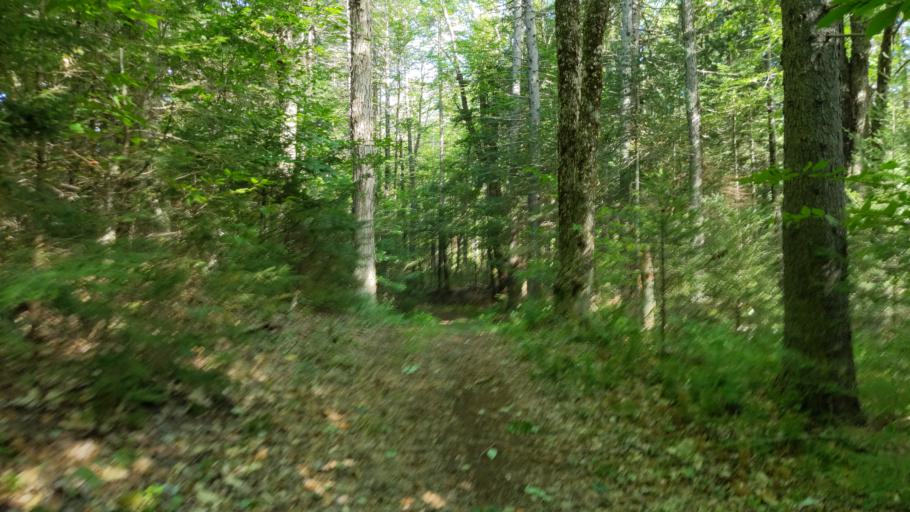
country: US
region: New Hampshire
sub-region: Sullivan County
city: Grantham
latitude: 43.5088
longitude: -72.1000
